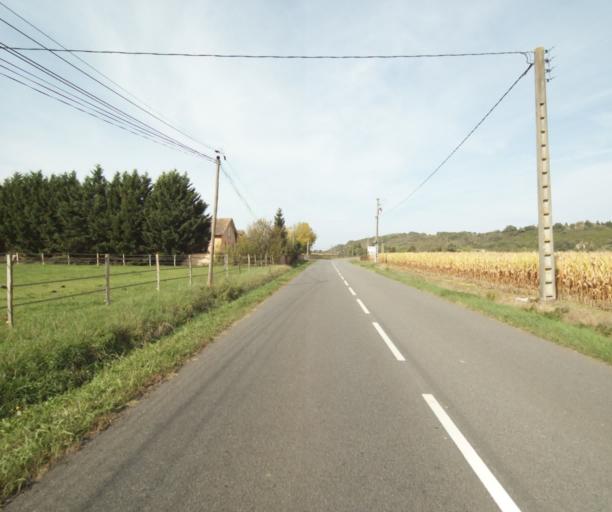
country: FR
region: Midi-Pyrenees
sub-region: Departement du Tarn-et-Garonne
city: Corbarieu
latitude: 43.9295
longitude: 1.3836
